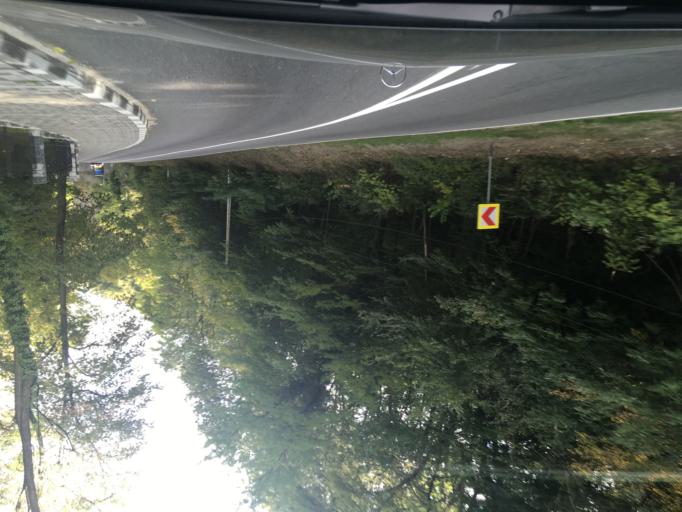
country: RO
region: Valcea
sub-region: Oras Calimanesti
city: Calimanesti
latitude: 45.2601
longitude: 24.3194
